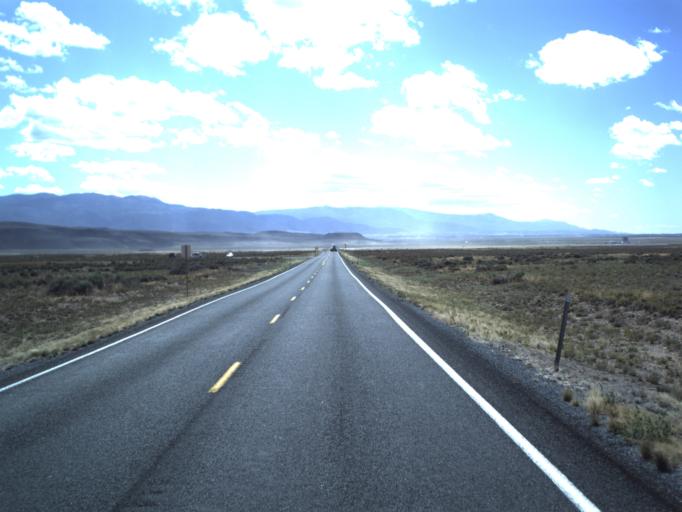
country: US
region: Utah
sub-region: Iron County
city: Enoch
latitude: 37.9142
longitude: -113.0315
